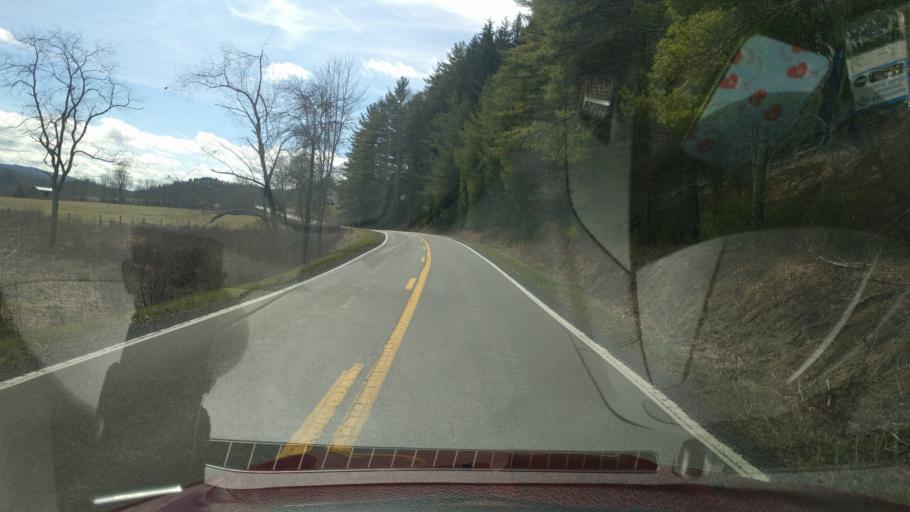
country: US
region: West Virginia
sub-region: Pocahontas County
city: Marlinton
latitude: 38.2234
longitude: -79.9176
